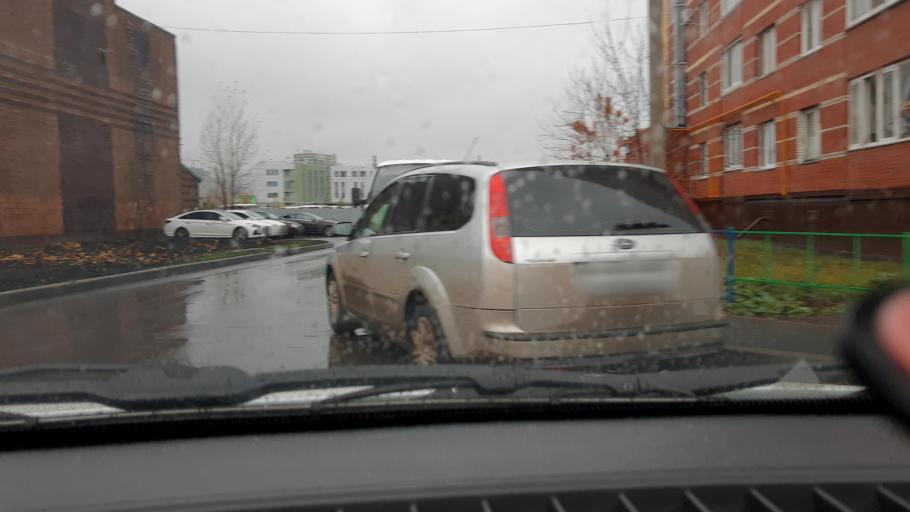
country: RU
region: Bashkortostan
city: Ufa
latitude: 54.7794
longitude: 56.0758
